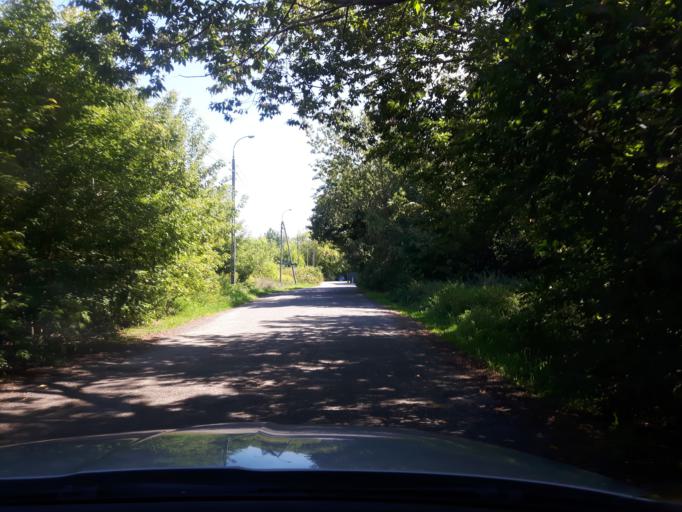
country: PL
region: Masovian Voivodeship
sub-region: Warszawa
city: Praga Poludnie
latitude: 52.2710
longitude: 21.0838
